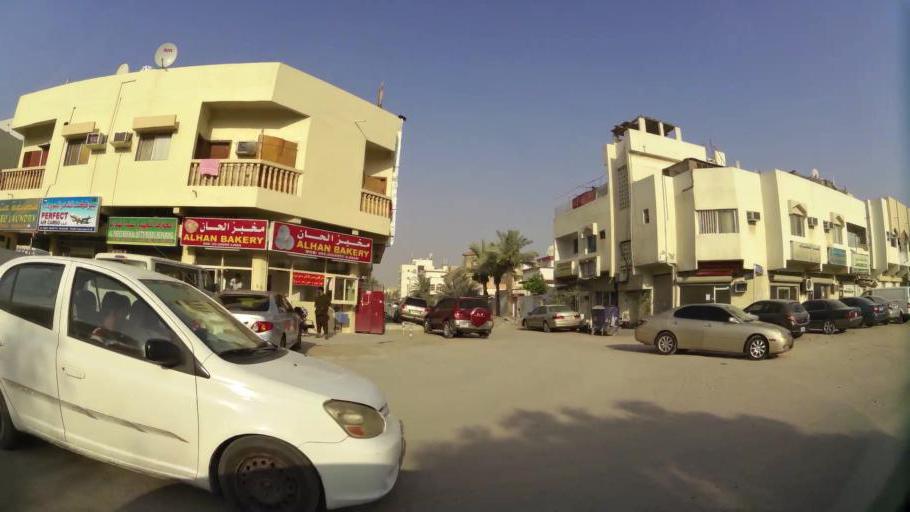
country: AE
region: Ajman
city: Ajman
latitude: 25.3855
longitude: 55.4476
